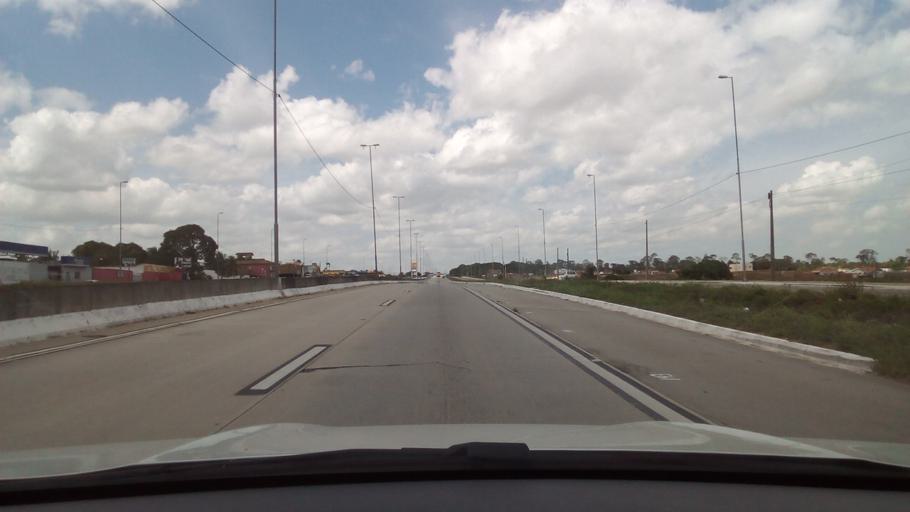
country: BR
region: Paraiba
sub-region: Mamanguape
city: Mamanguape
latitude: -6.8334
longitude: -35.1370
